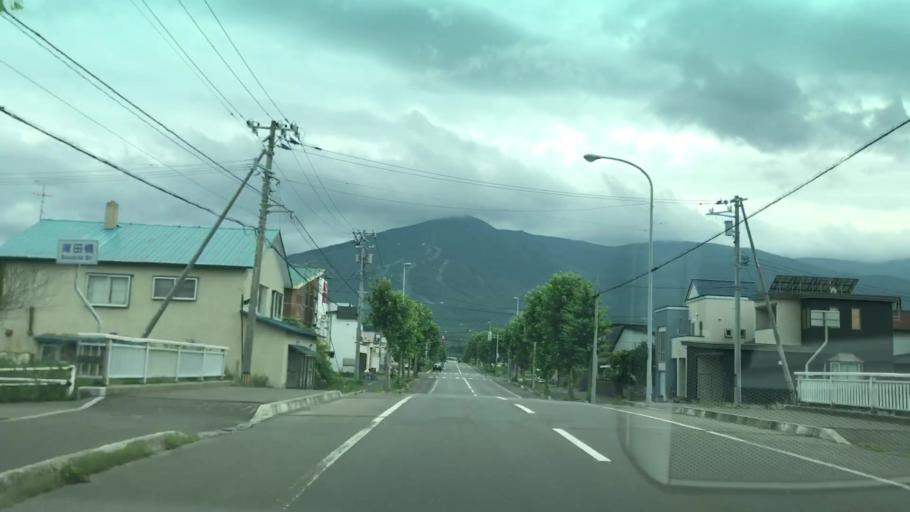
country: JP
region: Hokkaido
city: Iwanai
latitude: 42.9782
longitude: 140.5101
